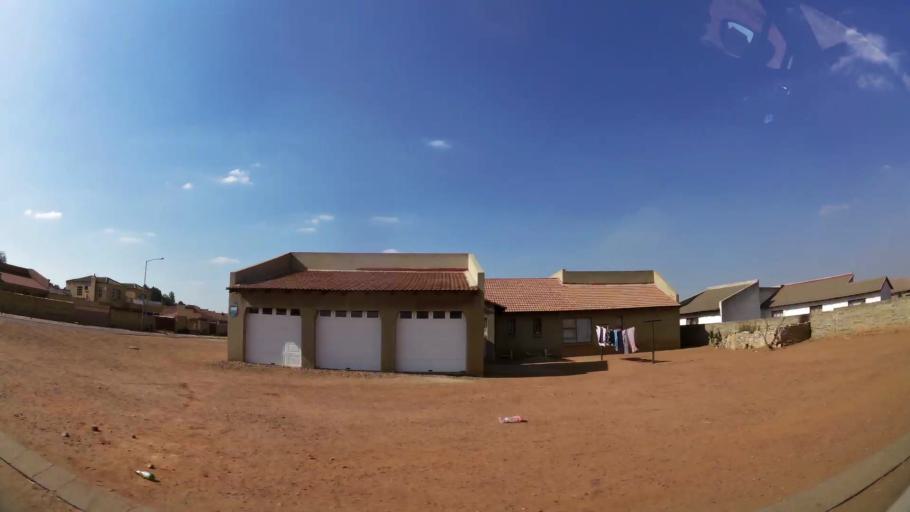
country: ZA
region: Gauteng
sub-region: City of Johannesburg Metropolitan Municipality
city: Roodepoort
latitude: -26.1666
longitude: 27.8019
